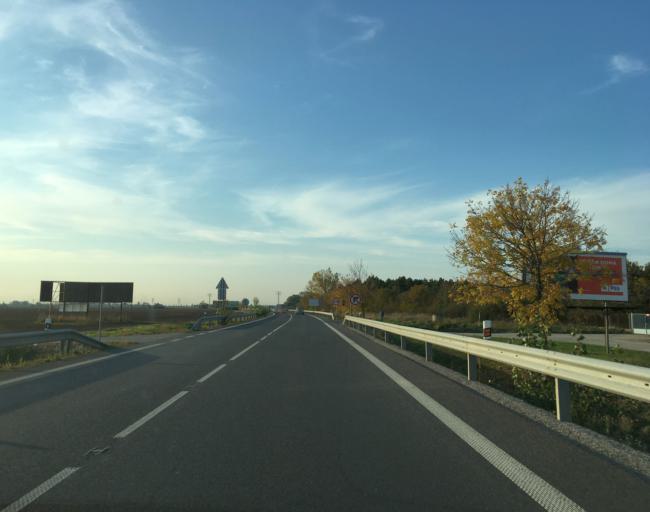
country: SK
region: Trnavsky
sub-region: Okres Galanta
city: Galanta
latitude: 48.1941
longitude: 17.6913
